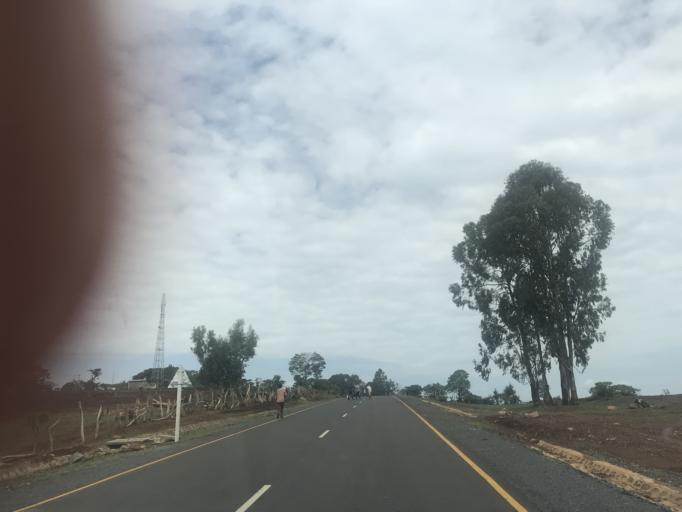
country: ET
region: Oromiya
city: Shambu
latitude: 9.8690
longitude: 36.6911
